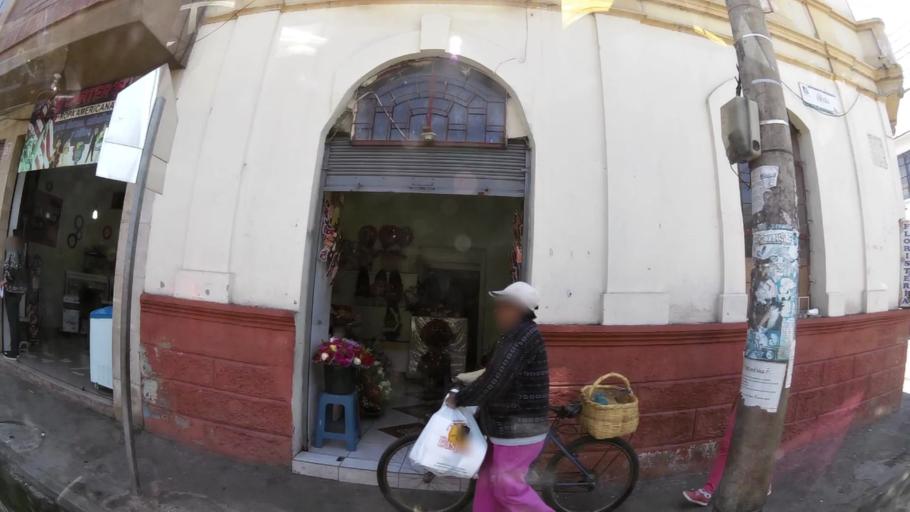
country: EC
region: Chimborazo
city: Riobamba
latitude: -1.6735
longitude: -78.6523
